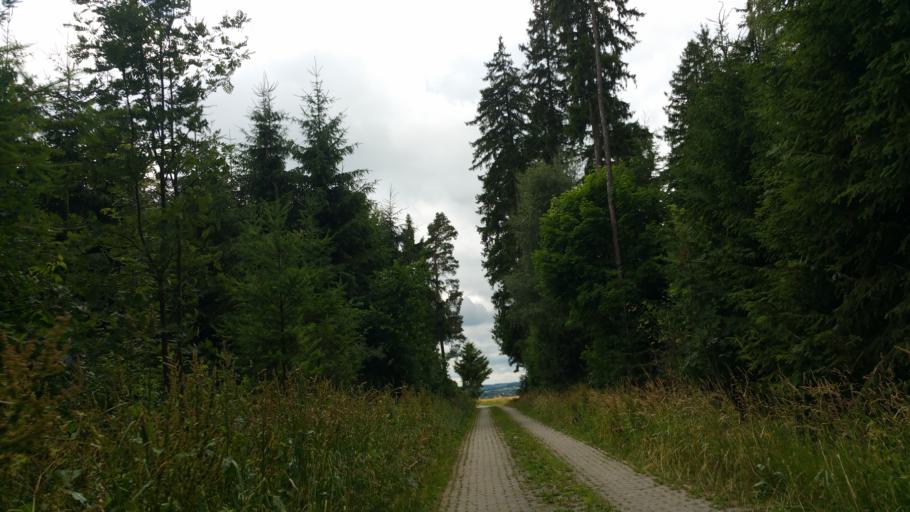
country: DE
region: Bavaria
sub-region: Upper Franconia
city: Schwarzenbach an der Saale
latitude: 50.2296
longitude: 11.9759
